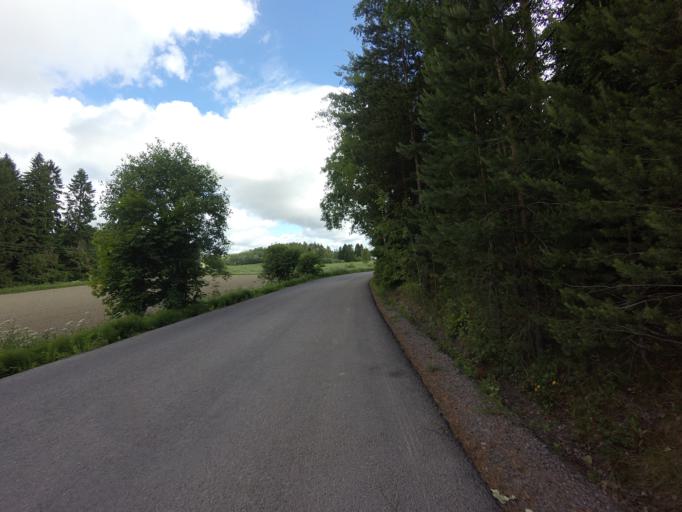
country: FI
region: Uusimaa
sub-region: Helsinki
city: Espoo
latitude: 60.1668
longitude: 24.5978
